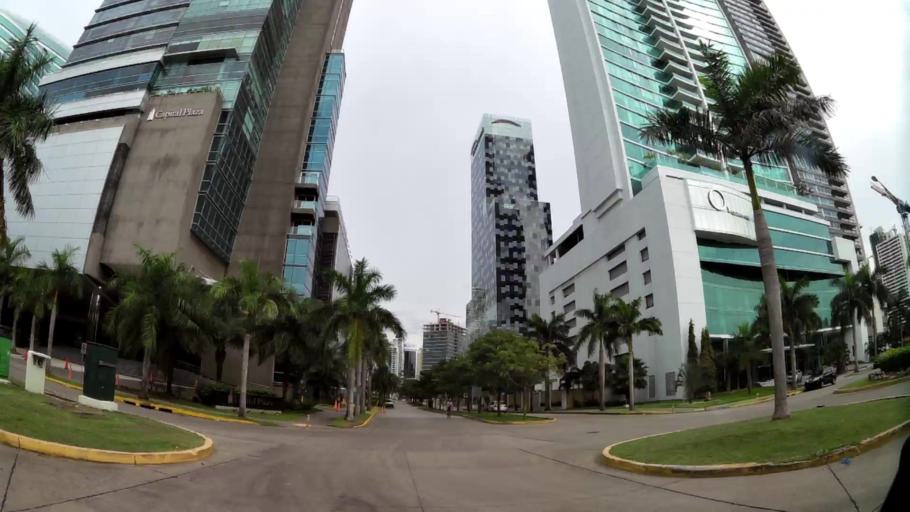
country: PA
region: Panama
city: San Miguelito
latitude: 9.0080
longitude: -79.4756
